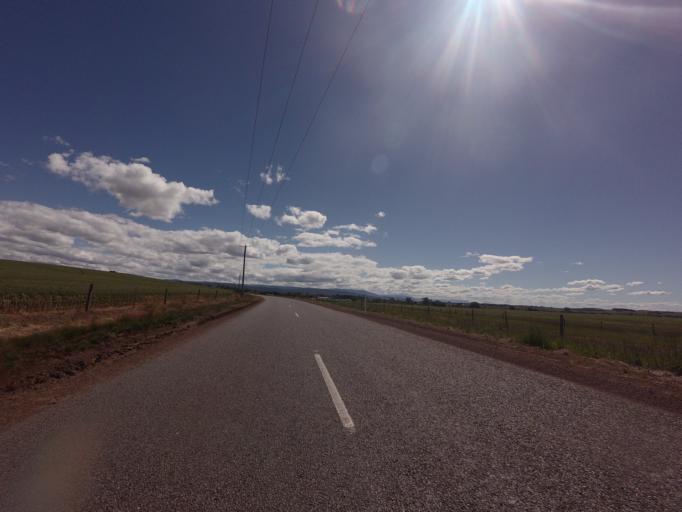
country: AU
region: Tasmania
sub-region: Northern Midlands
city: Evandale
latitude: -41.9395
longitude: 147.5470
